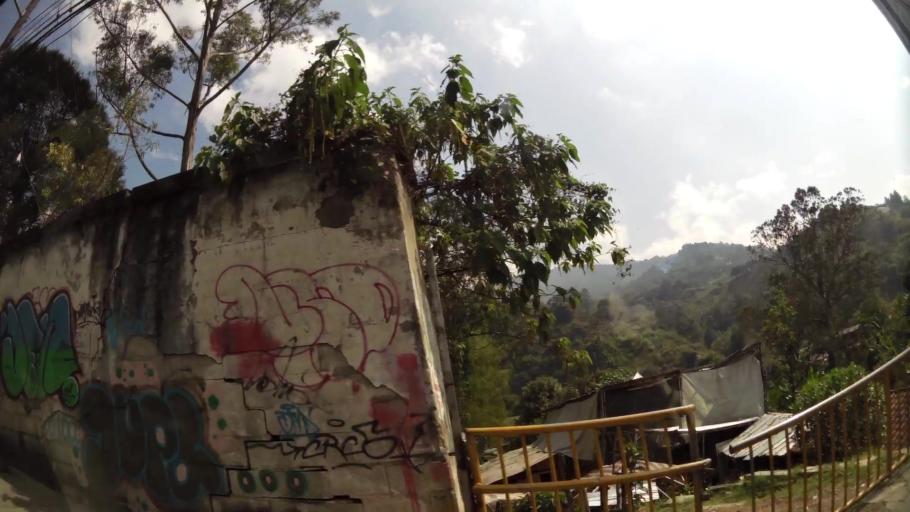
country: CO
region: Antioquia
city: La Estrella
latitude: 6.1799
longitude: -75.6387
